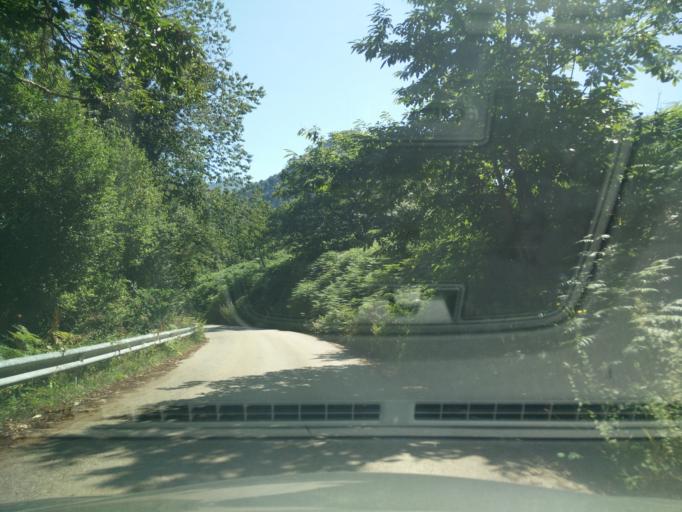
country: ES
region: Asturias
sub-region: Province of Asturias
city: Amieva
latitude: 43.1950
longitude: -5.1293
